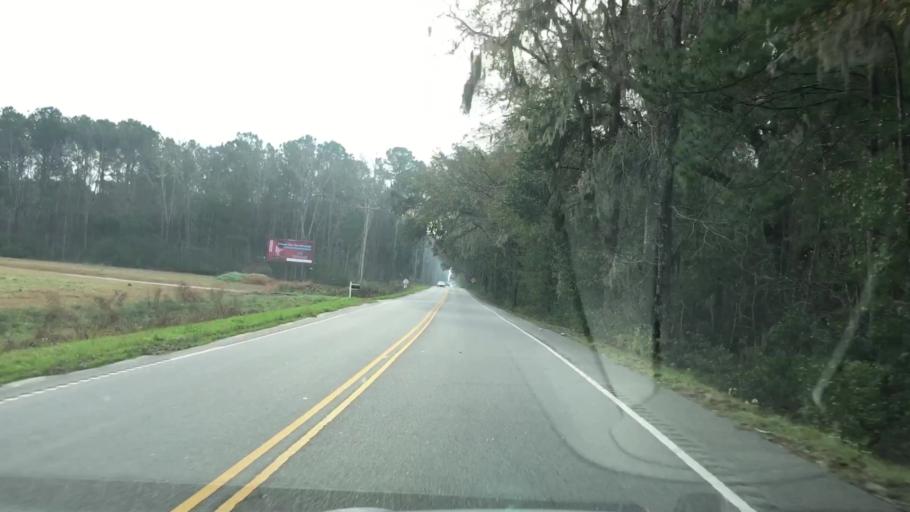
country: US
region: South Carolina
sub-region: Jasper County
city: Ridgeland
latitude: 32.5396
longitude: -80.9112
